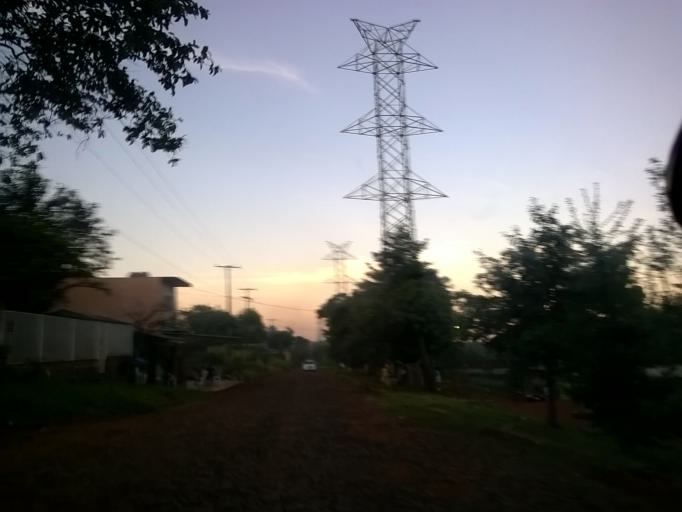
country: PY
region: Alto Parana
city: Ciudad del Este
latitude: -25.4832
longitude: -54.6452
